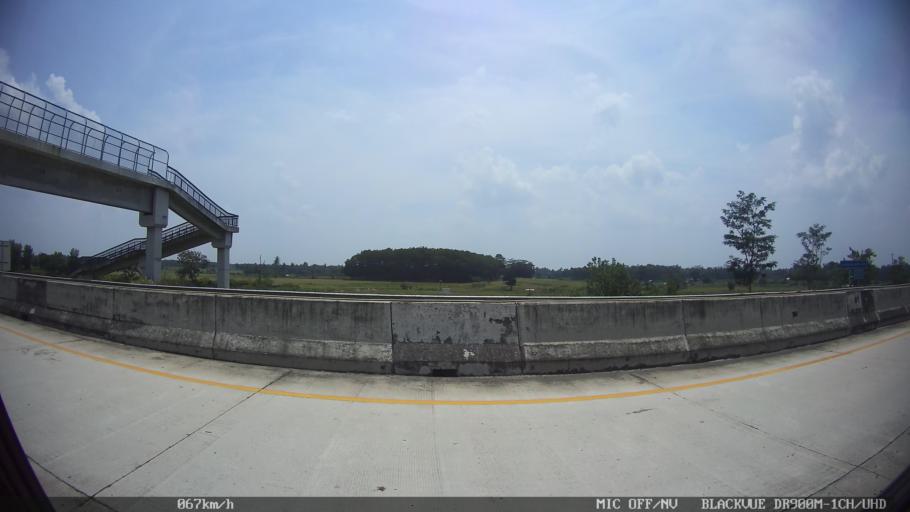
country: ID
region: Lampung
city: Natar
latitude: -5.2853
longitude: 105.2200
